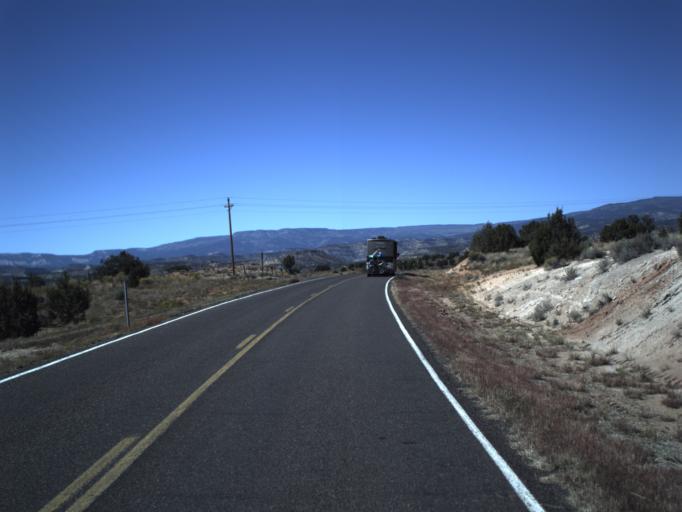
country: US
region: Utah
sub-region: Wayne County
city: Loa
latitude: 37.7424
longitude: -111.5583
